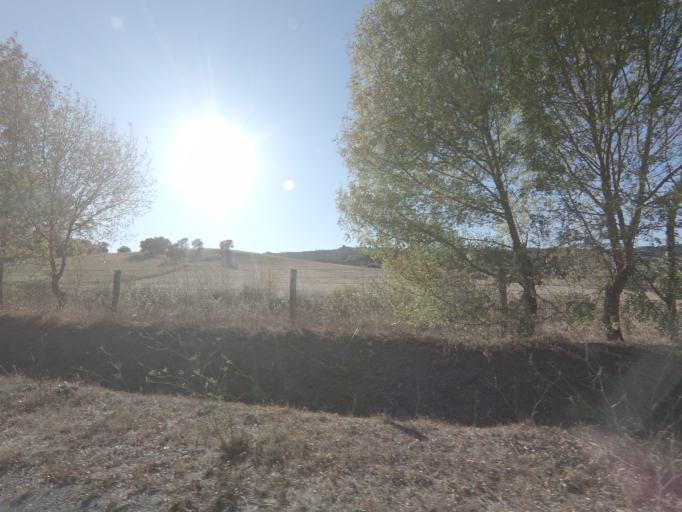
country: PT
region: Setubal
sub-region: Palmela
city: Quinta do Anjo
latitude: 38.5144
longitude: -8.9711
